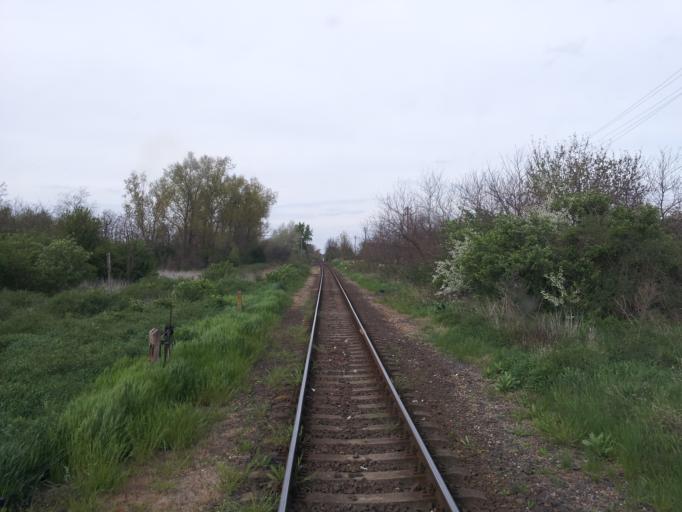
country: HU
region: Komarom-Esztergom
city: Nagyigmand
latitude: 47.6339
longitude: 18.0516
